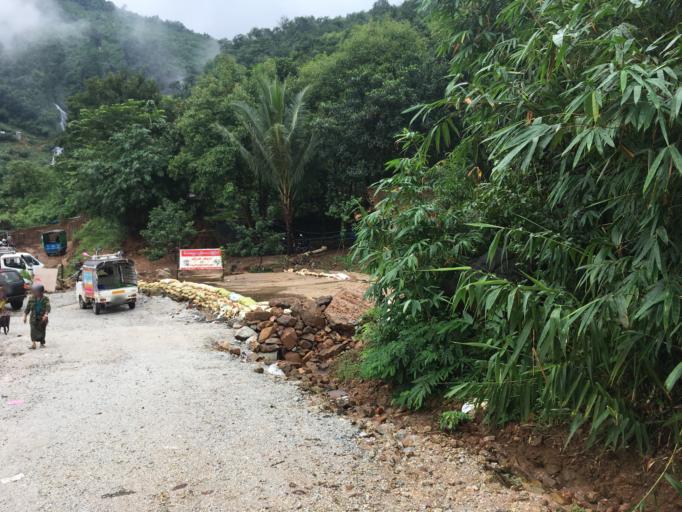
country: MM
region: Mon
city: Martaban
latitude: 16.6715
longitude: 97.5105
